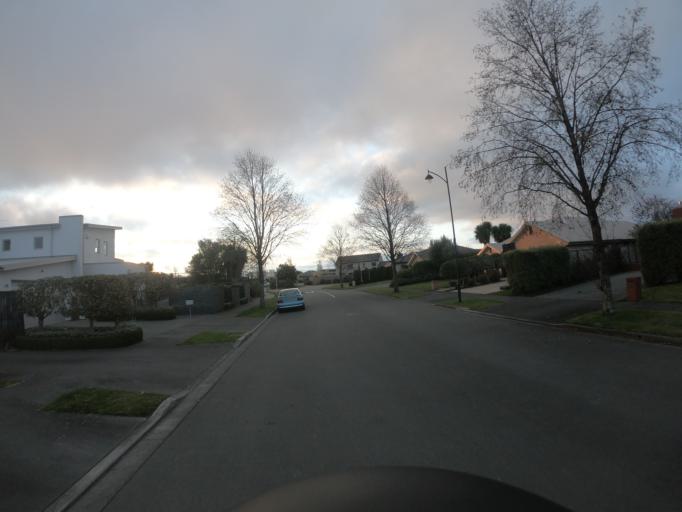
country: NZ
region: Canterbury
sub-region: Selwyn District
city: Prebbleton
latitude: -43.5598
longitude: 172.5607
